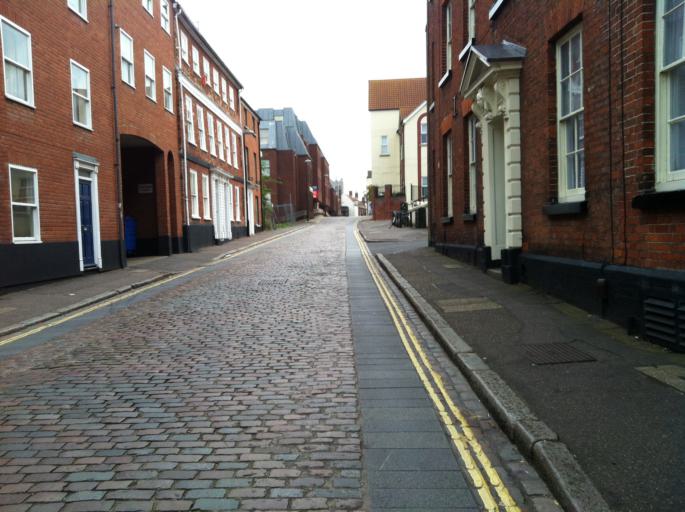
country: GB
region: England
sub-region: Norfolk
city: Norwich
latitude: 52.6304
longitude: 1.2891
